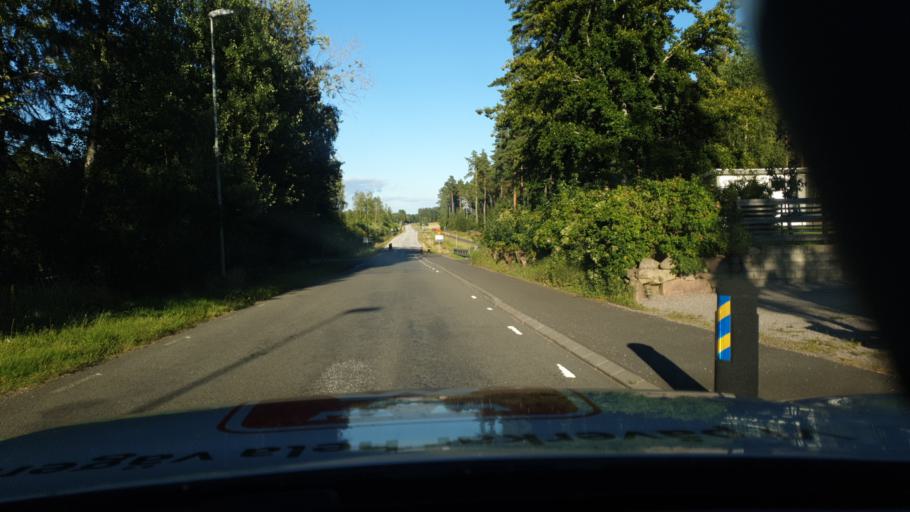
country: SE
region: Vaestra Goetaland
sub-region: Skovde Kommun
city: Stopen
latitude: 58.4794
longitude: 13.8676
